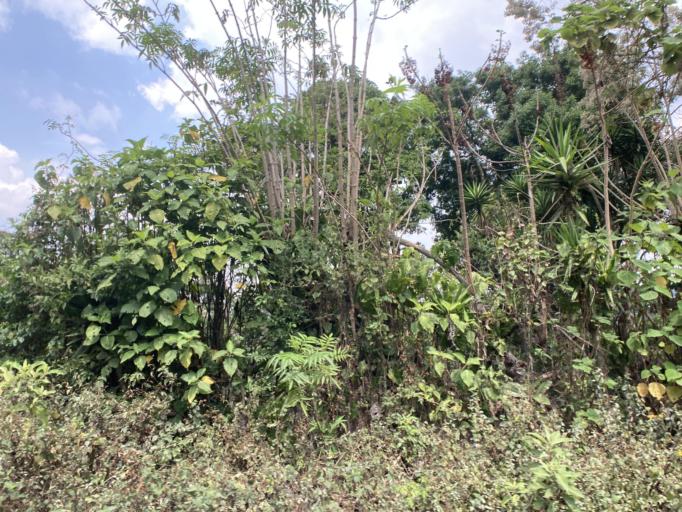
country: GT
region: Guatemala
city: Villa Canales
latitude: 14.4144
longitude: -90.5317
